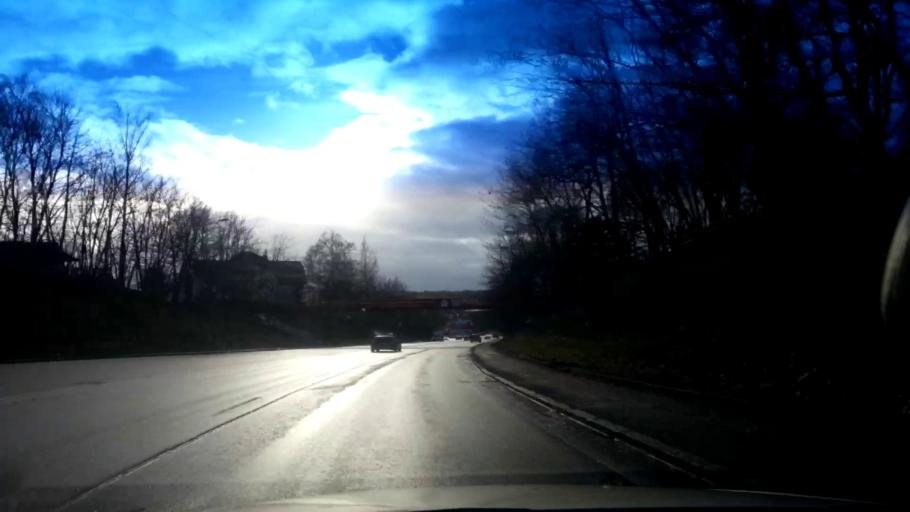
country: CZ
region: Karlovarsky
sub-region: Okres Cheb
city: Cheb
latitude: 50.0883
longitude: 12.3709
